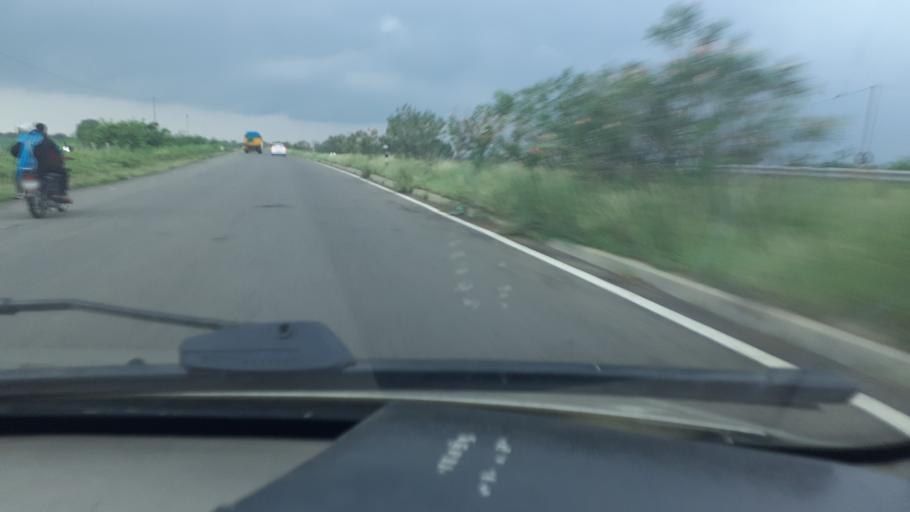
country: IN
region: Tamil Nadu
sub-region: Thoothukkudi
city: Kovilpatti
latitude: 9.1199
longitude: 77.8165
